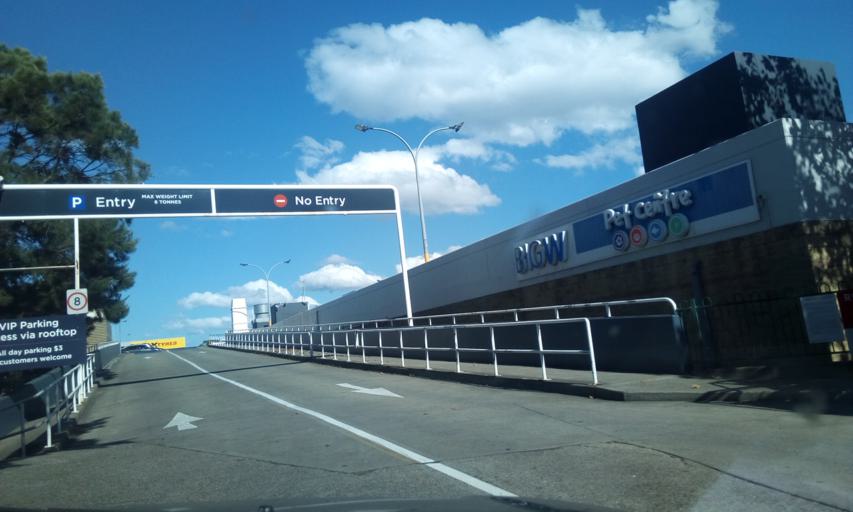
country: AU
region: New South Wales
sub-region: Wollongong
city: Port Kembla
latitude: -34.4854
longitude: 150.8908
